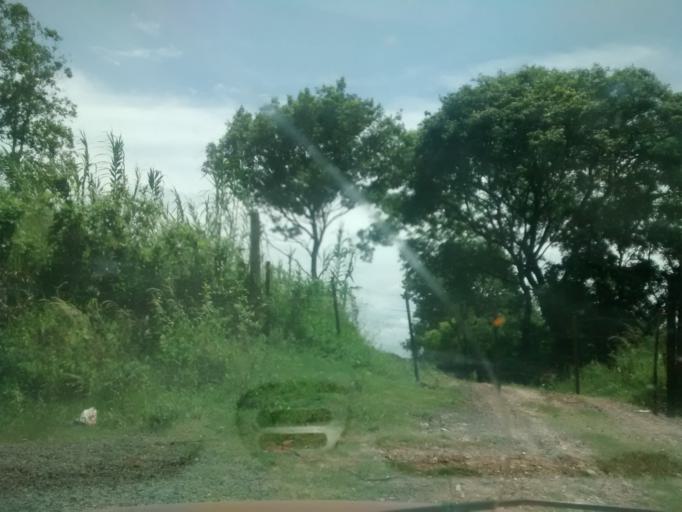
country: AR
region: Chaco
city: Resistencia
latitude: -27.4326
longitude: -58.9753
